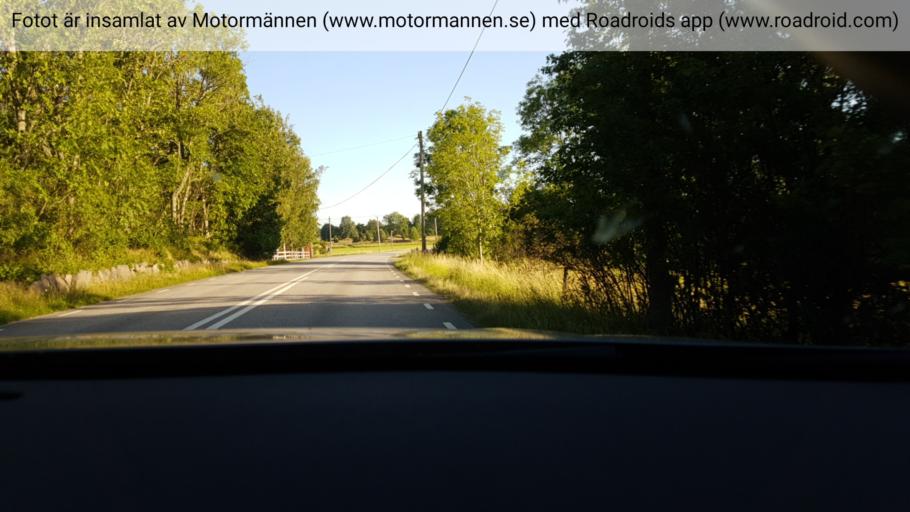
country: SE
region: Vaestra Goetaland
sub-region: Skovde Kommun
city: Stopen
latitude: 58.5186
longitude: 13.9787
